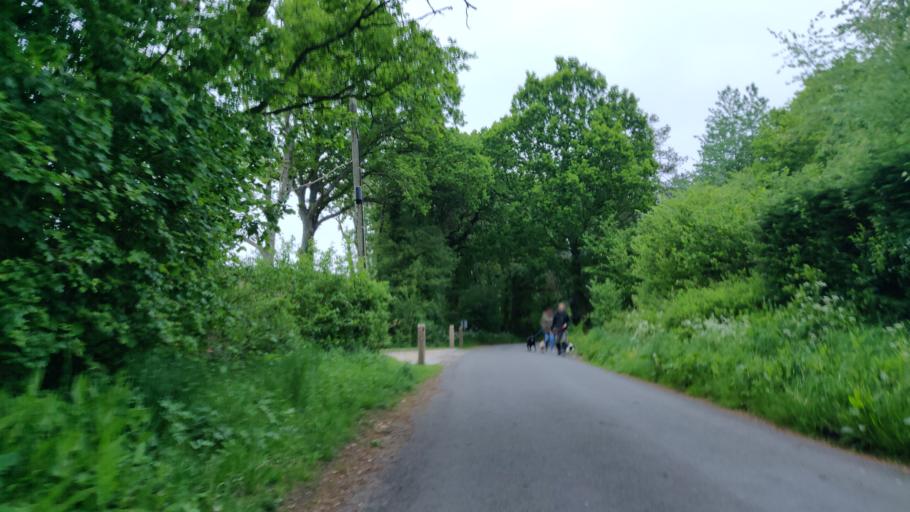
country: GB
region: England
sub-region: West Sussex
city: Southwater
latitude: 51.0374
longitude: -0.3356
